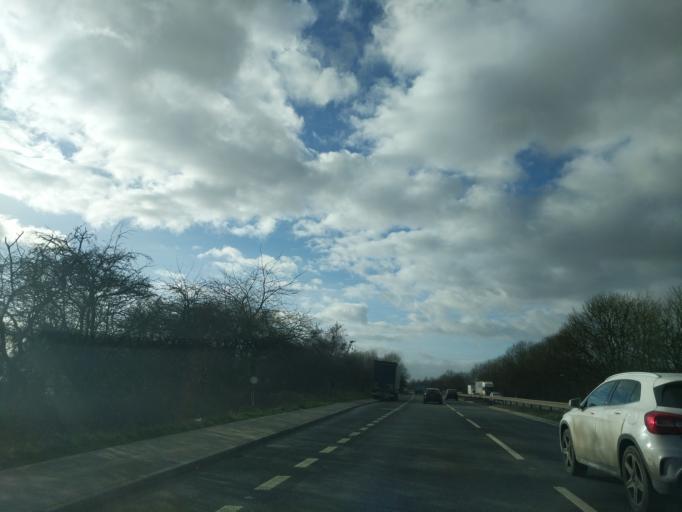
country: GB
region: England
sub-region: Derbyshire
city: Alfreton
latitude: 53.0928
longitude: -1.3586
